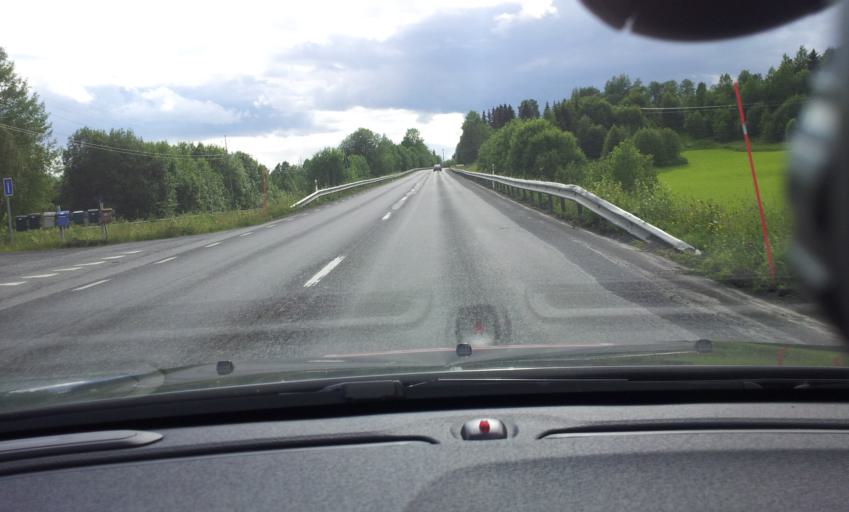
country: SE
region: Jaemtland
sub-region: Are Kommun
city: Jarpen
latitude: 63.3233
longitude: 13.3683
